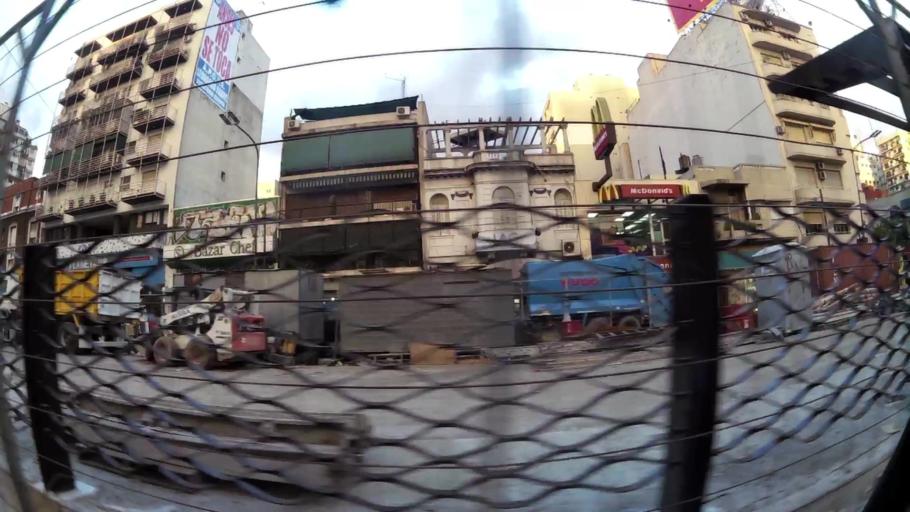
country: AR
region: Buenos Aires F.D.
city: Colegiales
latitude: -34.5580
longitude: -58.4603
